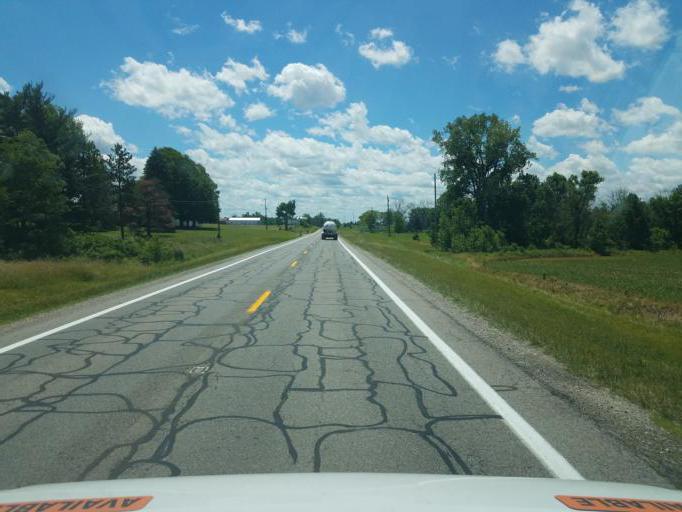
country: US
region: Ohio
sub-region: Crawford County
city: Galion
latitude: 40.6529
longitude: -82.8219
